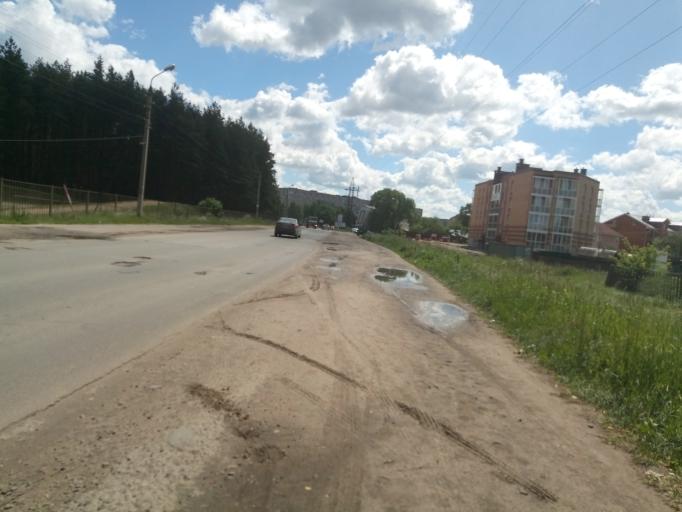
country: RU
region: Jaroslavl
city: Yaroslavl
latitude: 57.6590
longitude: 39.9625
